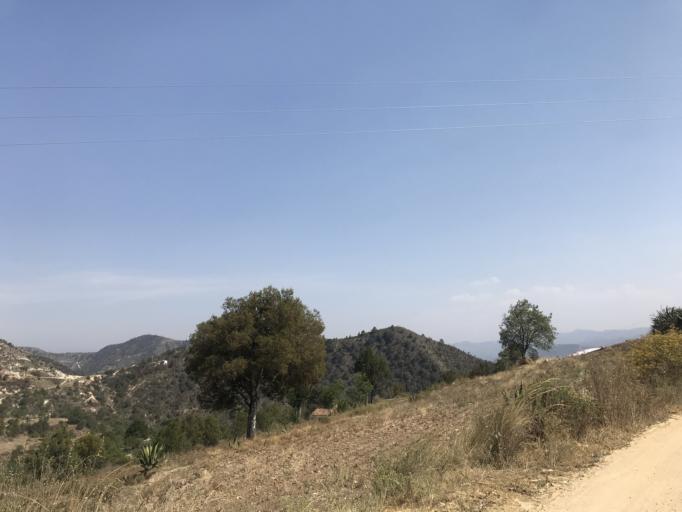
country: MX
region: Puebla
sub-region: Zautla
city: San Andres Yahuitlalpan
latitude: 19.6927
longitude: -97.8481
